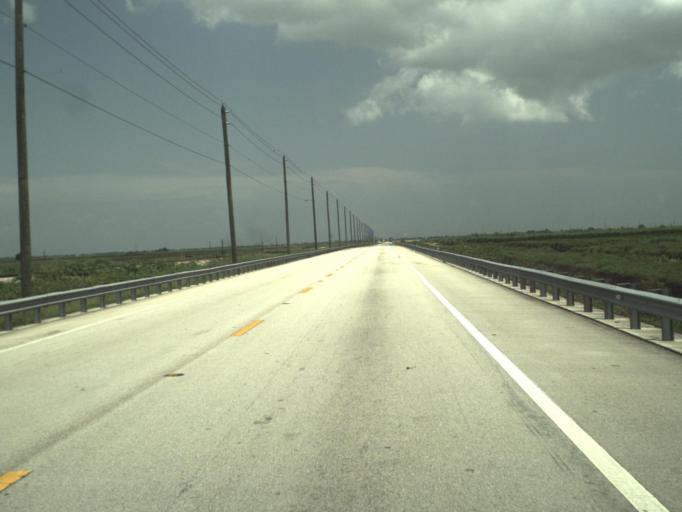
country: US
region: Florida
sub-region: Palm Beach County
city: Pahokee
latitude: 26.7593
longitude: -80.6597
